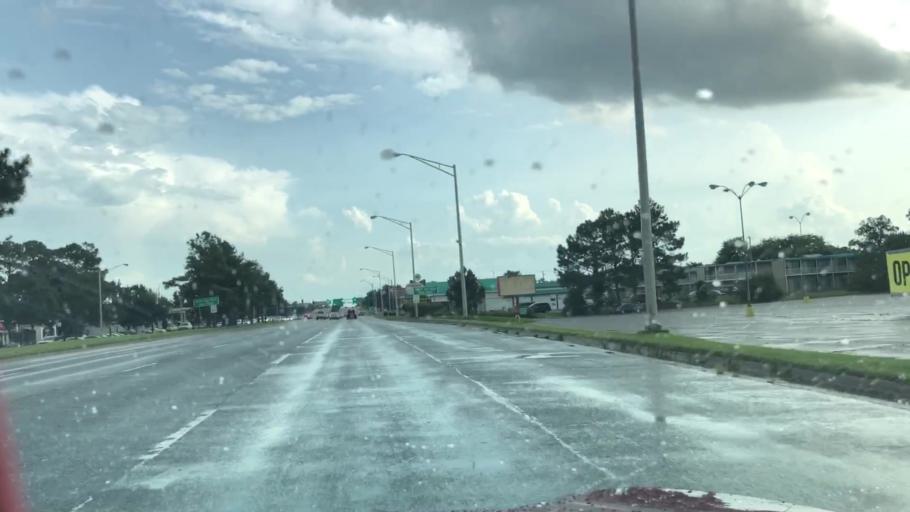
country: US
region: Virginia
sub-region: City of Chesapeake
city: Chesapeake
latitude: 36.8514
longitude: -76.2102
